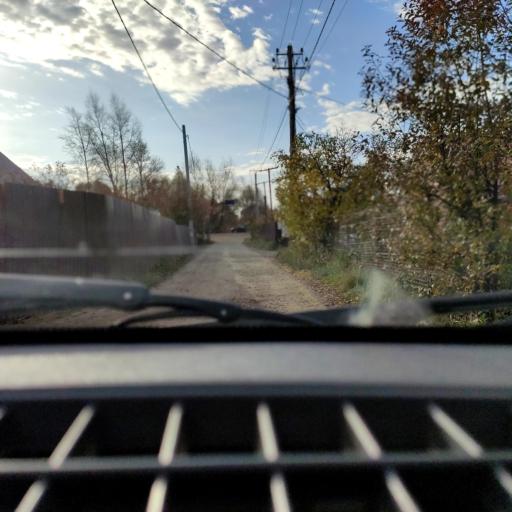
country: RU
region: Bashkortostan
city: Avdon
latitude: 54.7132
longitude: 55.8150
